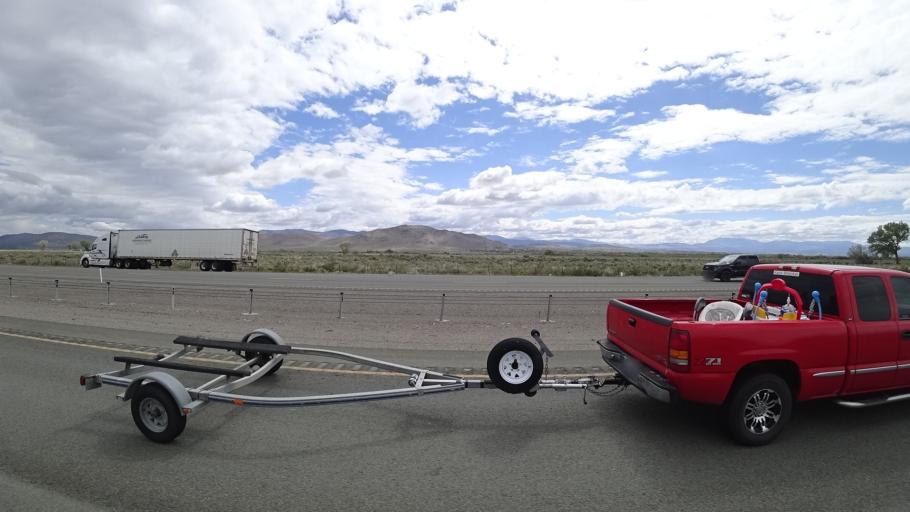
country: US
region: Nevada
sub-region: Douglas County
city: Indian Hills
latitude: 39.0582
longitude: -119.7801
